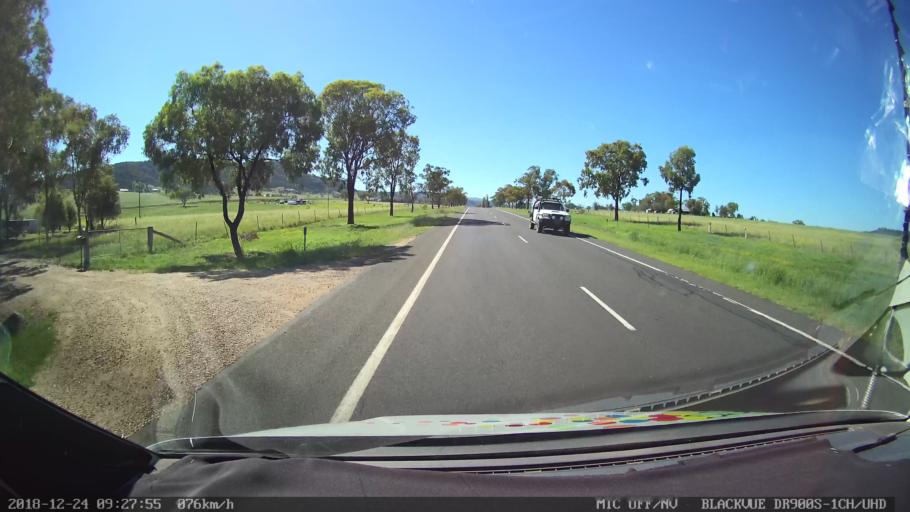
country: AU
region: New South Wales
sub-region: Liverpool Plains
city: Quirindi
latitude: -31.5325
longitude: 150.6846
